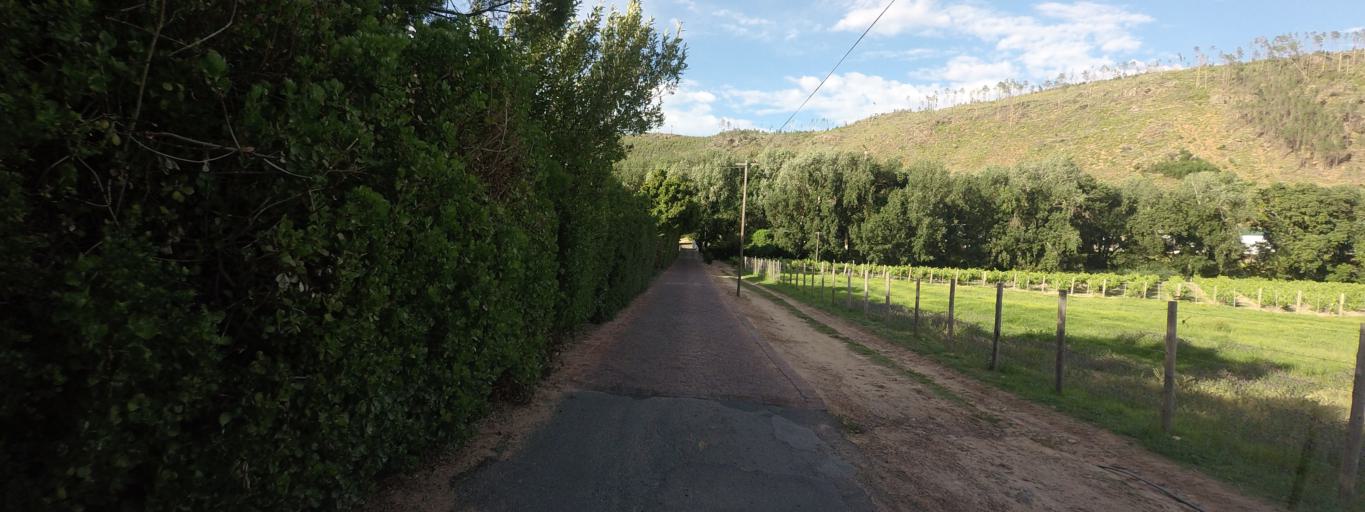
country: ZA
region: Western Cape
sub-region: Cape Winelands District Municipality
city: Paarl
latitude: -33.8981
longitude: 19.0939
